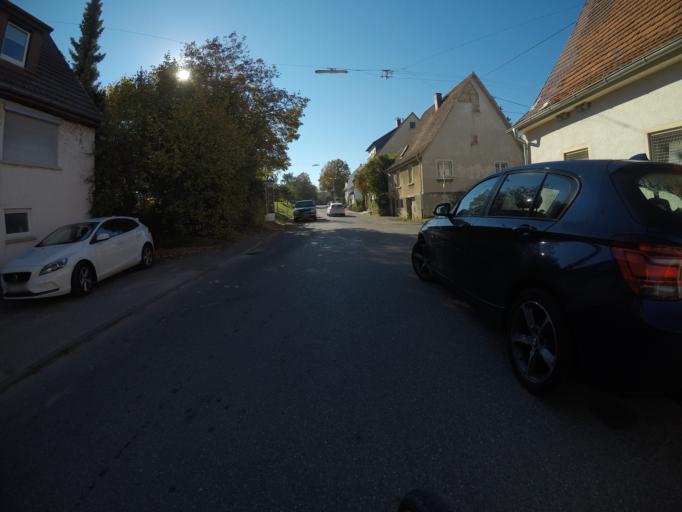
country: DE
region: Baden-Wuerttemberg
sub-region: Regierungsbezirk Stuttgart
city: Filderstadt
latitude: 48.6500
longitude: 9.2188
